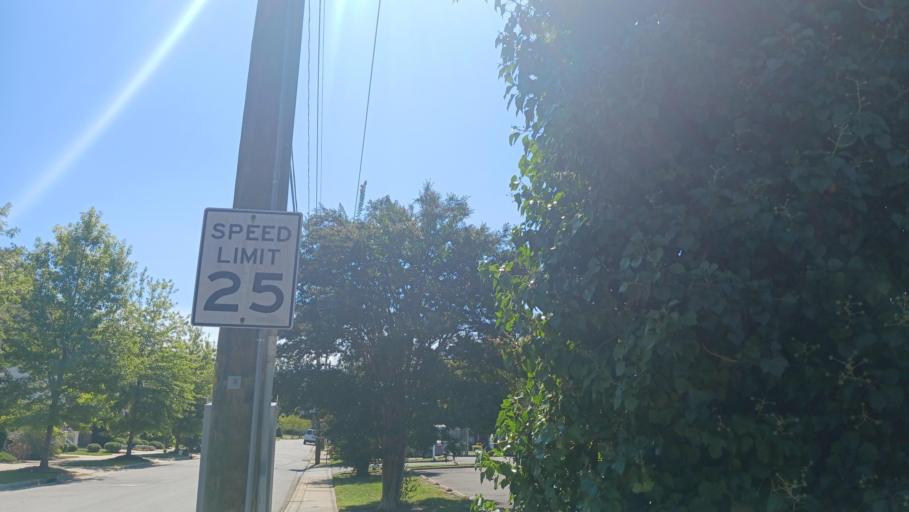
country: US
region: North Carolina
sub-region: Mecklenburg County
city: Charlotte
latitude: 35.2093
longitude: -80.8319
